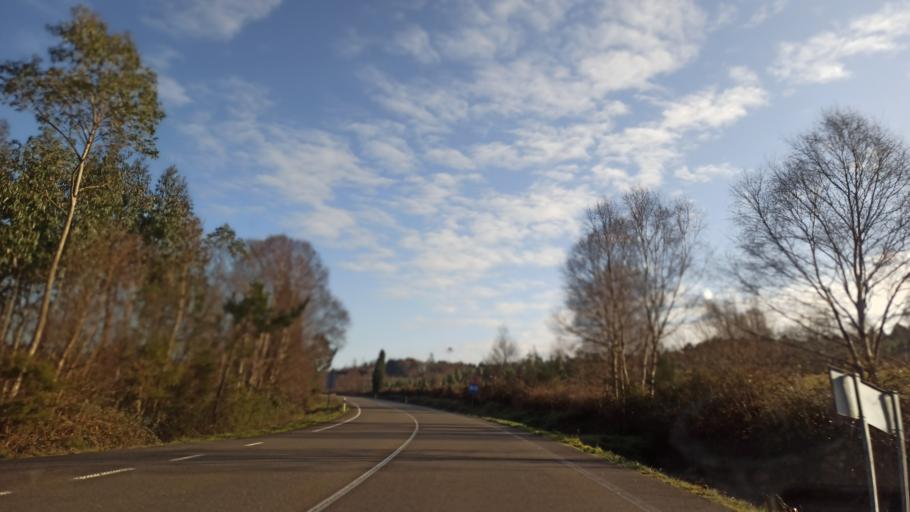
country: ES
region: Galicia
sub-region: Provincia da Coruna
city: As Pontes de Garcia Rodriguez
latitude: 43.4843
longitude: -7.8415
